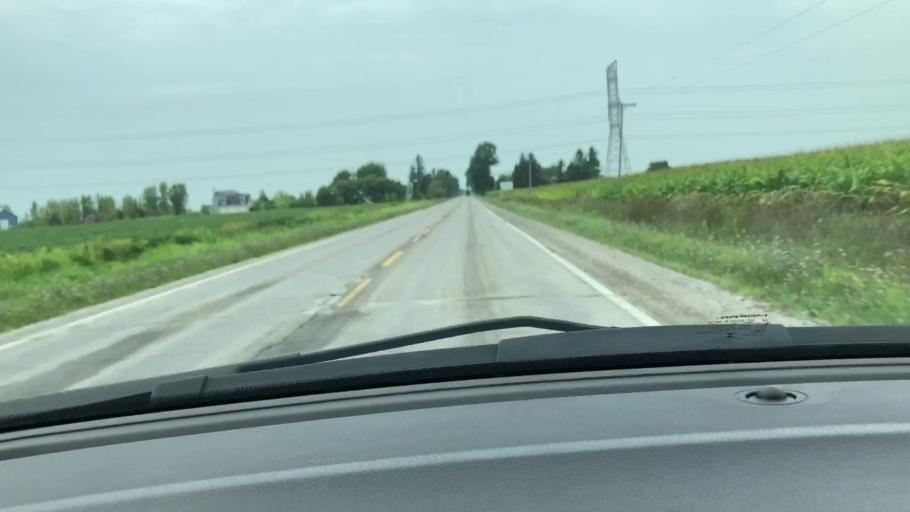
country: US
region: Michigan
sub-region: Saginaw County
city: Freeland
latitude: 43.5548
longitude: -84.0900
